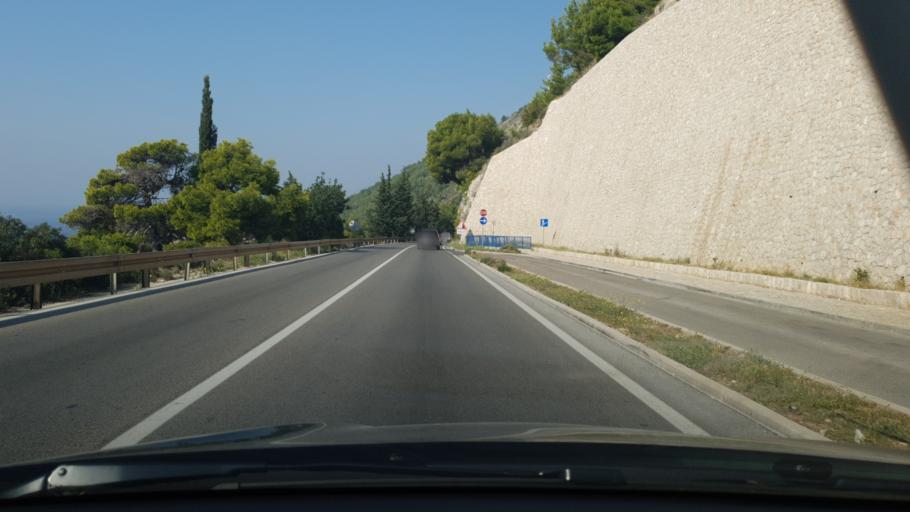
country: HR
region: Dubrovacko-Neretvanska
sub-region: Grad Dubrovnik
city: Dubrovnik
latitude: 42.6424
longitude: 18.1222
